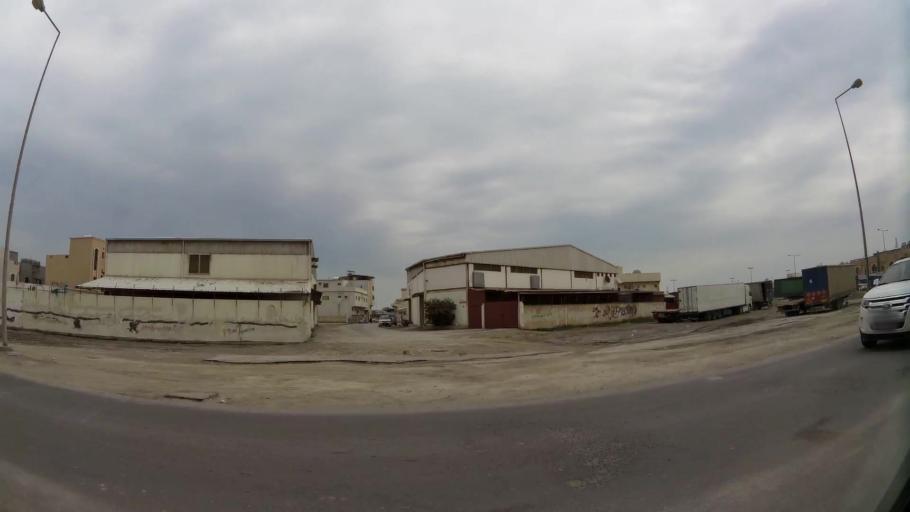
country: BH
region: Northern
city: Sitrah
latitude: 26.1660
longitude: 50.6127
